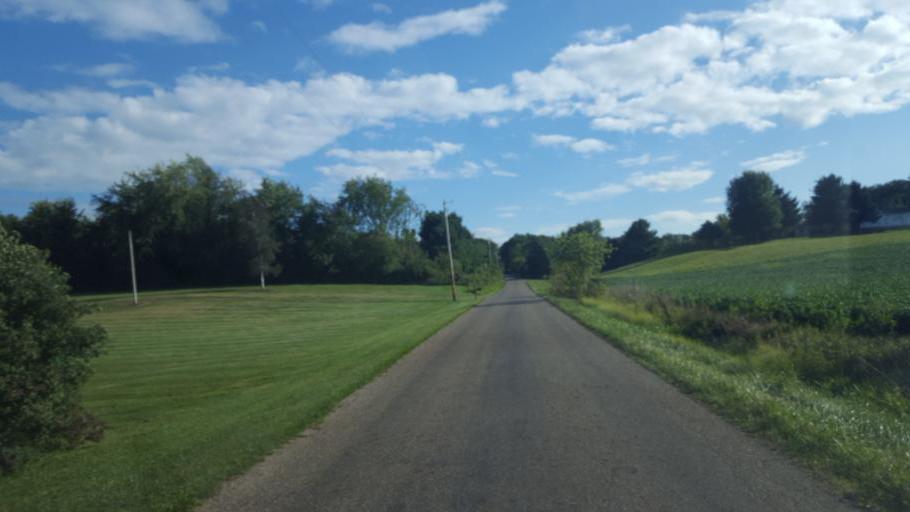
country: US
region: Ohio
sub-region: Knox County
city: Fredericktown
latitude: 40.4219
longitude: -82.5629
